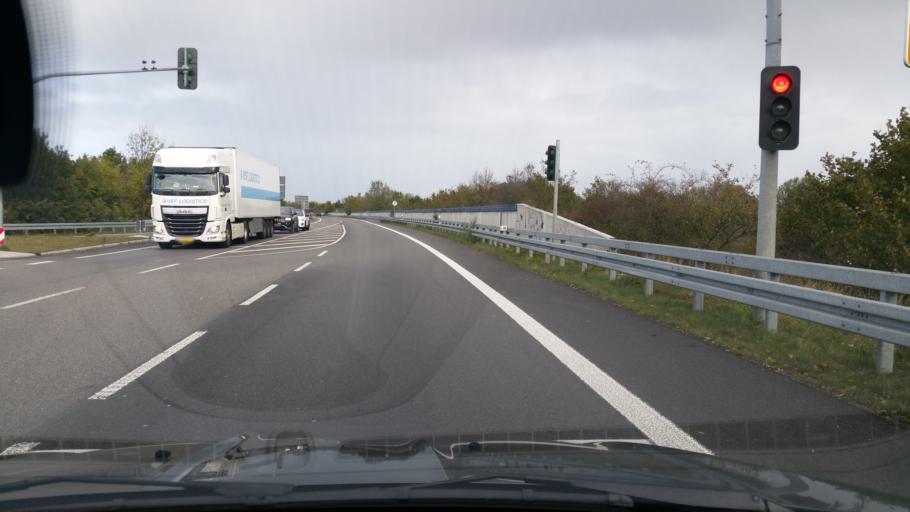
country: DE
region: North Rhine-Westphalia
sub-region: Regierungsbezirk Dusseldorf
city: Bocholt
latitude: 51.8181
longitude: 6.5976
